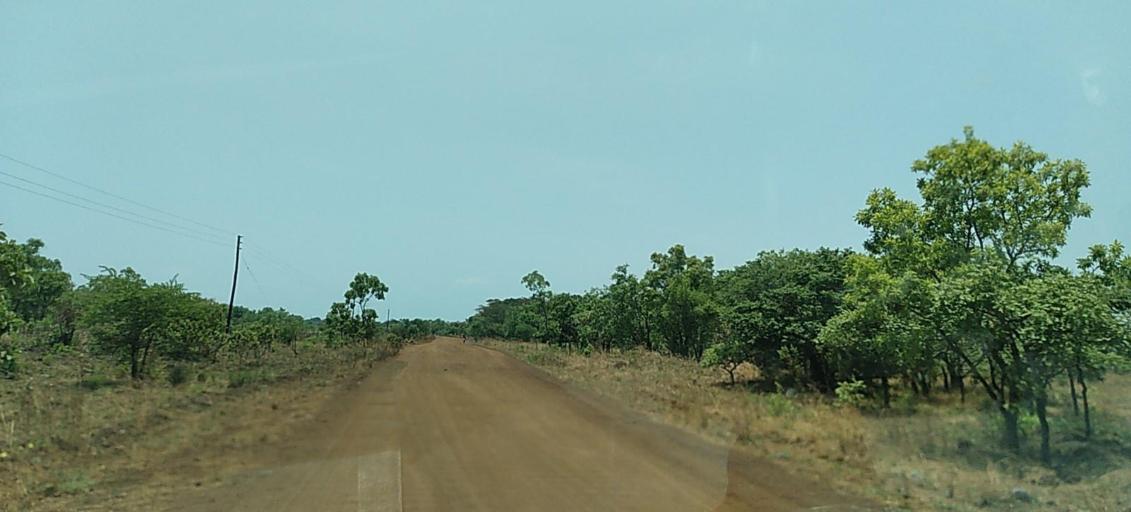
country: ZM
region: Copperbelt
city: Mpongwe
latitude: -13.7081
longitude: 27.8683
